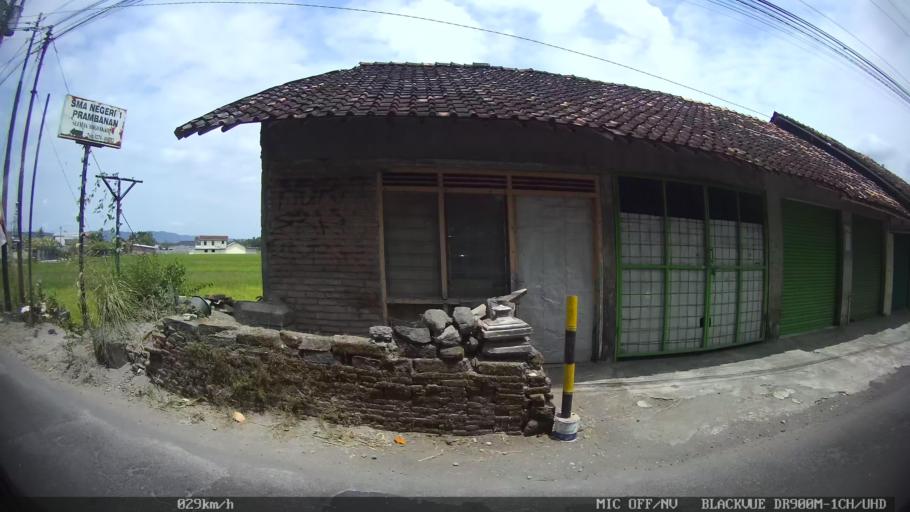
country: ID
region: Central Java
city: Candi Prambanan
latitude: -7.7837
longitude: 110.4782
